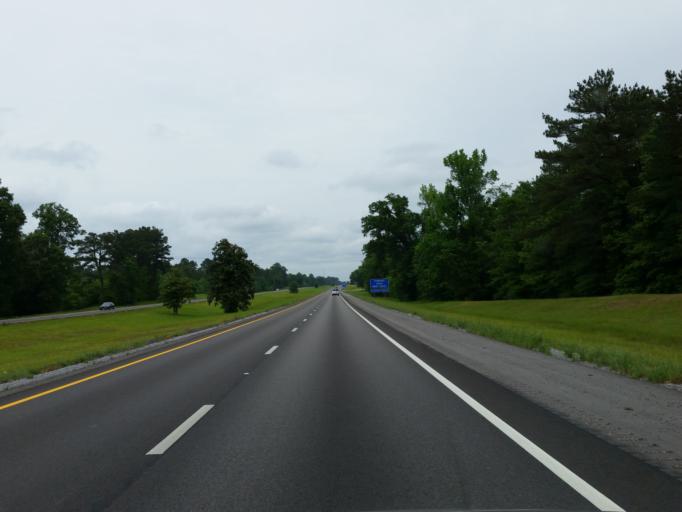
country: US
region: Mississippi
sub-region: Jones County
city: Sharon
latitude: 31.7974
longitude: -89.0541
